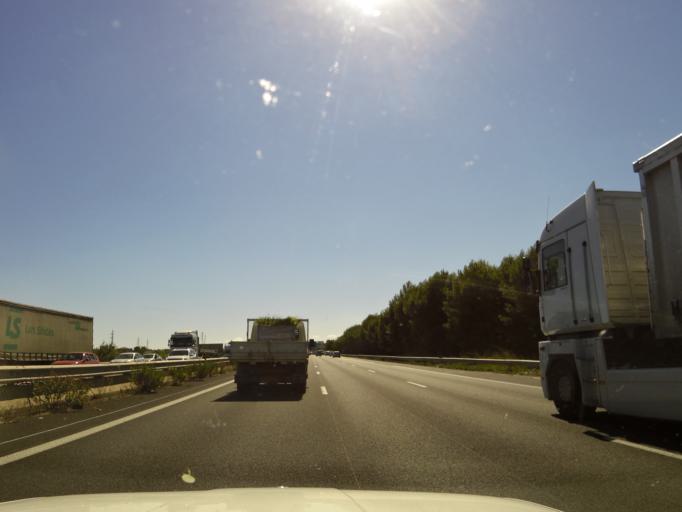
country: FR
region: Languedoc-Roussillon
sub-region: Departement de l'Herault
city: Lattes
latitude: 43.5797
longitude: 3.8834
